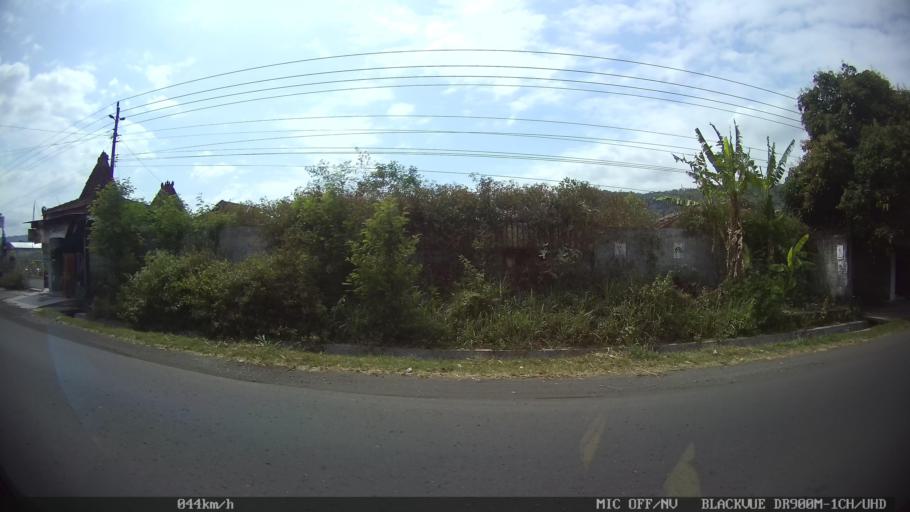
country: ID
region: Daerah Istimewa Yogyakarta
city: Depok
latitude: -7.8331
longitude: 110.4774
